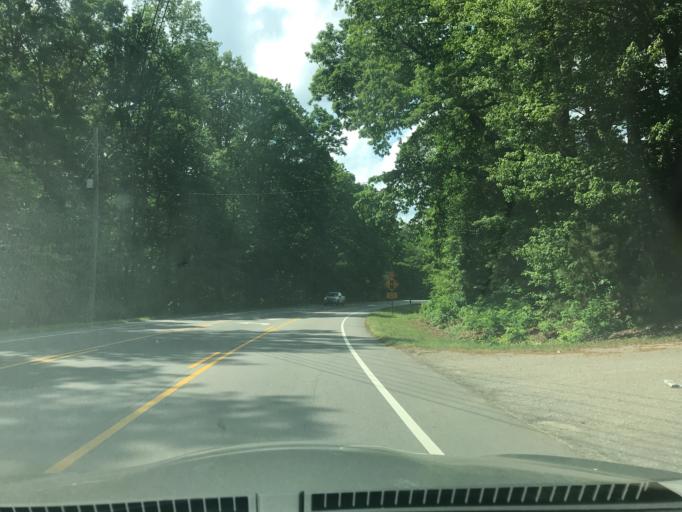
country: US
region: North Carolina
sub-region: Wake County
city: West Raleigh
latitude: 35.8830
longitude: -78.5990
